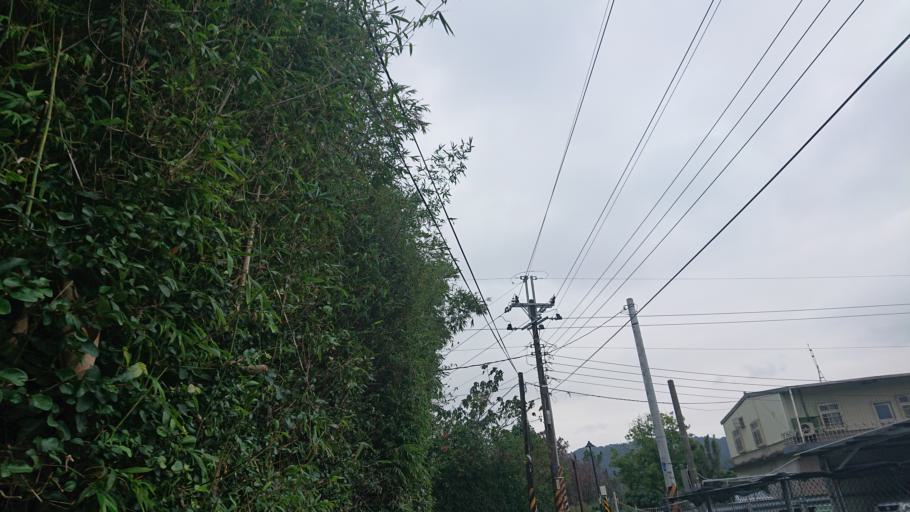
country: TW
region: Taiwan
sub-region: Taoyuan
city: Taoyuan
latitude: 24.9489
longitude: 121.3646
